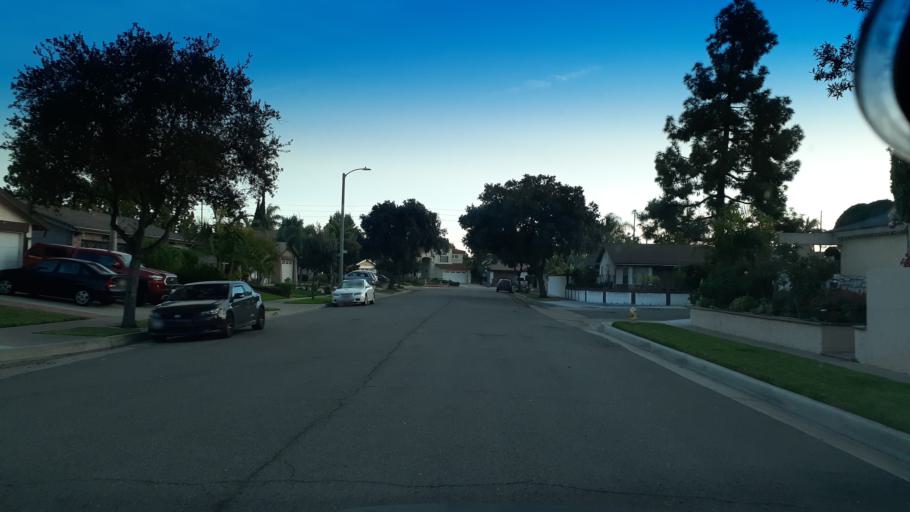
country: US
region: California
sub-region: Los Angeles County
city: Cerritos
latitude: 33.8553
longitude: -118.0765
